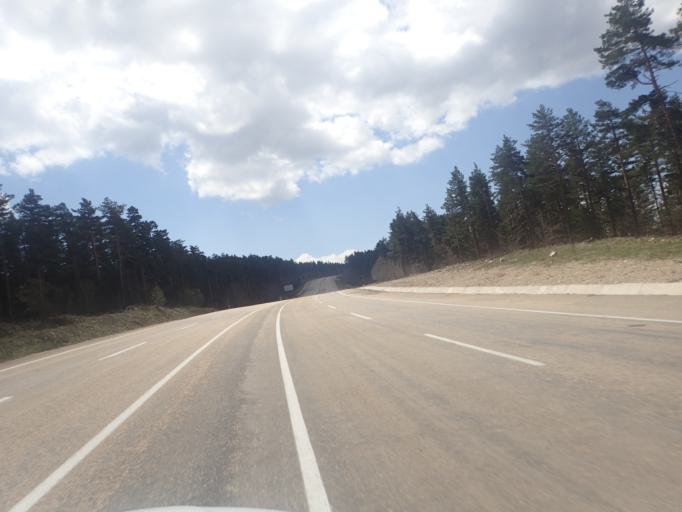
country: TR
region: Ordu
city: Mesudiye
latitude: 40.3843
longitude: 37.7778
